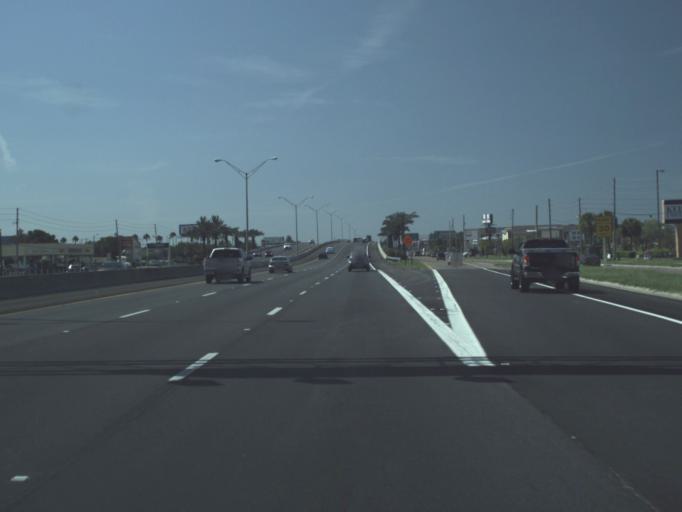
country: US
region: Florida
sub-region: Pinellas County
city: South Highpoint
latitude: 27.9206
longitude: -82.7303
